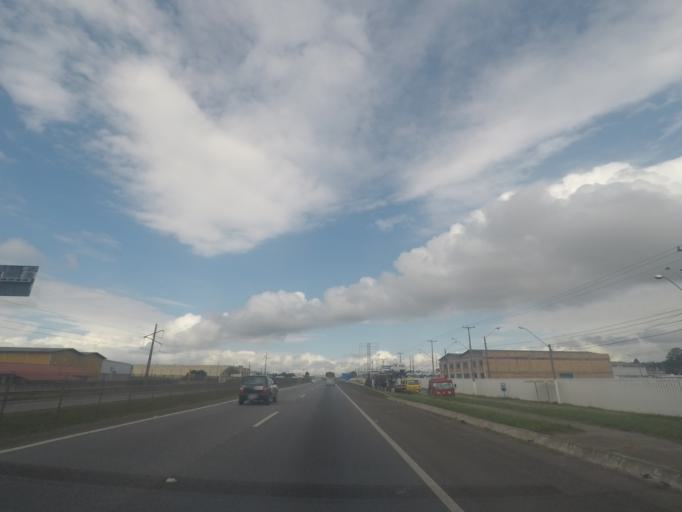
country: BR
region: Parana
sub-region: Piraquara
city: Piraquara
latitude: -25.5227
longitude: -49.1033
